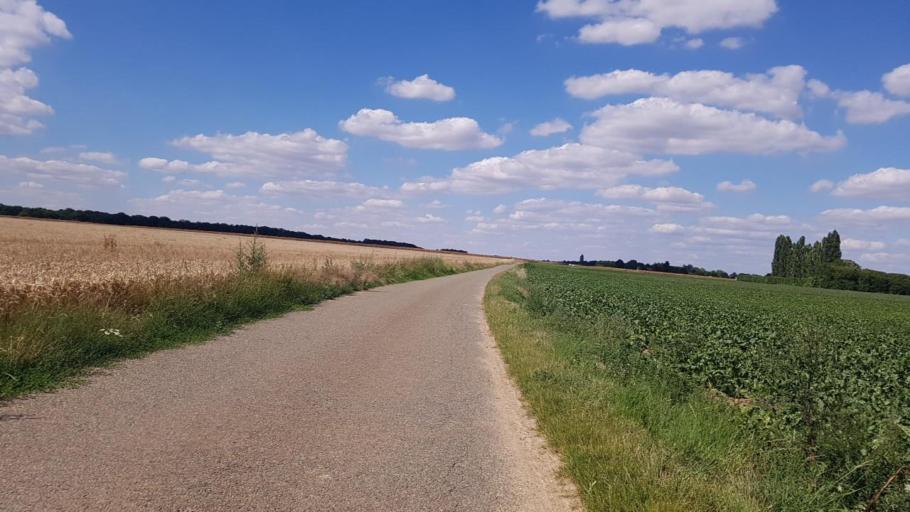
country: FR
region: Picardie
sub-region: Departement de l'Oise
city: Ver-sur-Launette
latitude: 49.0997
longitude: 2.6764
